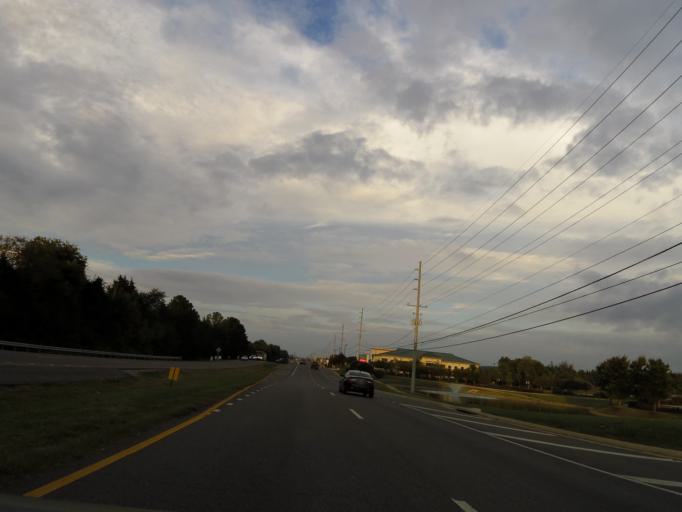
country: US
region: Alabama
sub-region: Madison County
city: Madison
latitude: 34.7490
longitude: -86.7662
